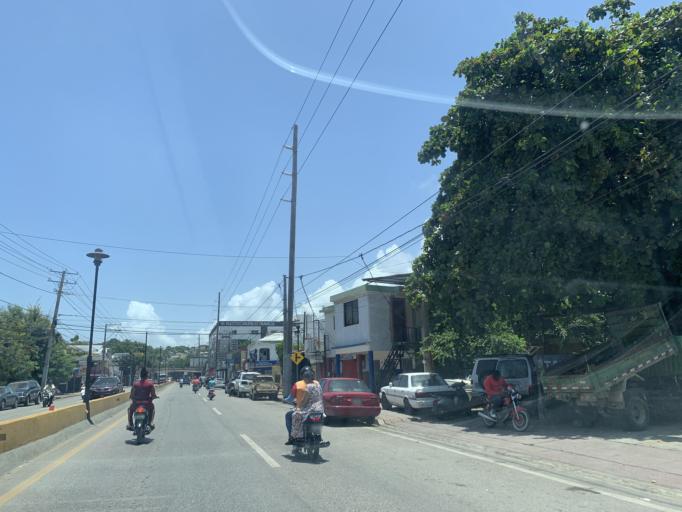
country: DO
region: Puerto Plata
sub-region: Puerto Plata
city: Puerto Plata
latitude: 19.7895
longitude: -70.6991
